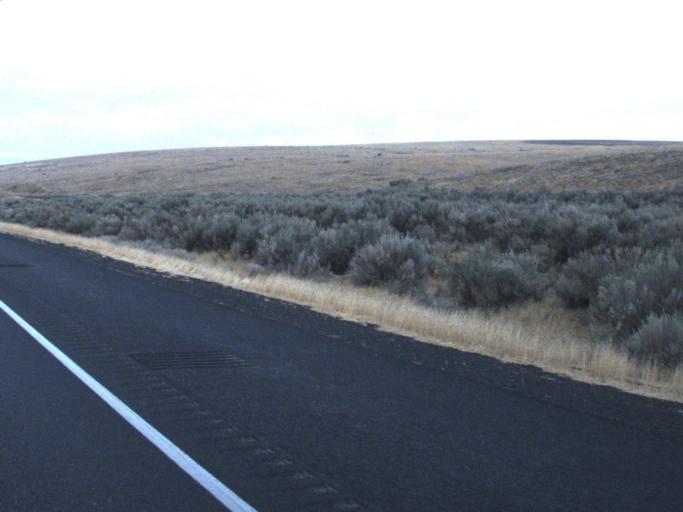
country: US
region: Washington
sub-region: Grant County
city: Warden
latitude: 47.0878
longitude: -118.8965
